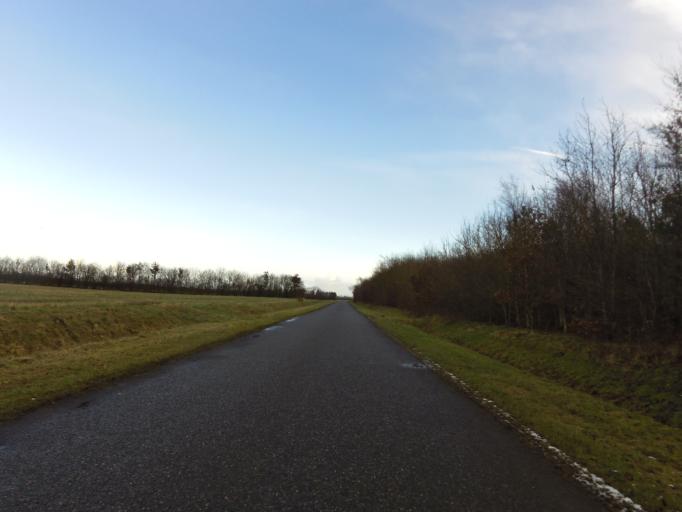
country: DK
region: South Denmark
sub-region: Haderslev Kommune
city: Gram
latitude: 55.2402
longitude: 9.0037
